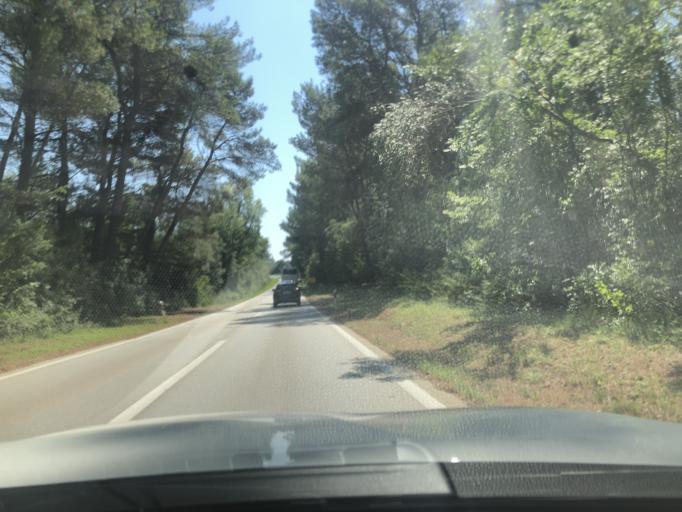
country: HR
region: Istarska
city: Vodnjan
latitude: 45.0337
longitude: 13.7918
